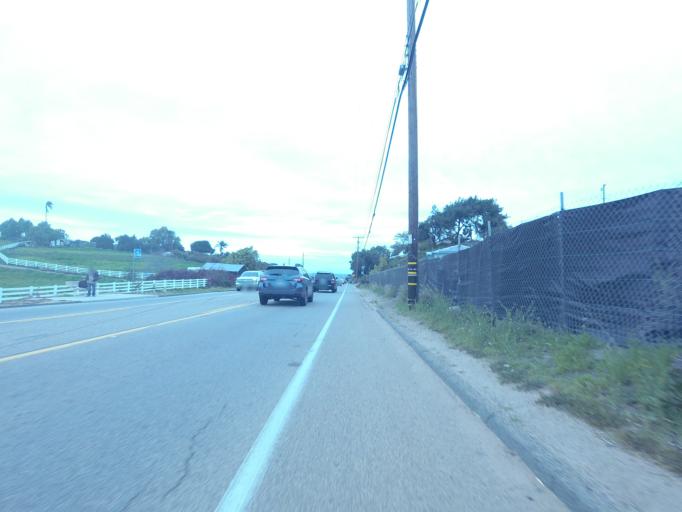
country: US
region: California
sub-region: San Diego County
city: Bonsall
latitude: 33.2434
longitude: -117.2263
